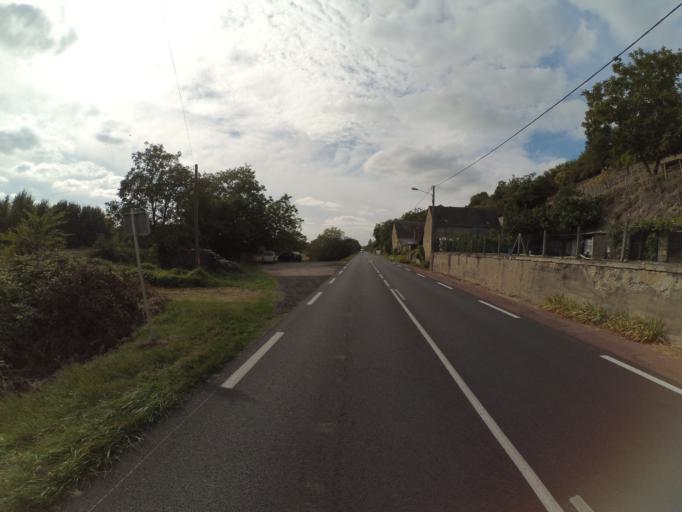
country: FR
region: Centre
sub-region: Departement d'Indre-et-Loire
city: Langeais
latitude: 47.3180
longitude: 0.3910
